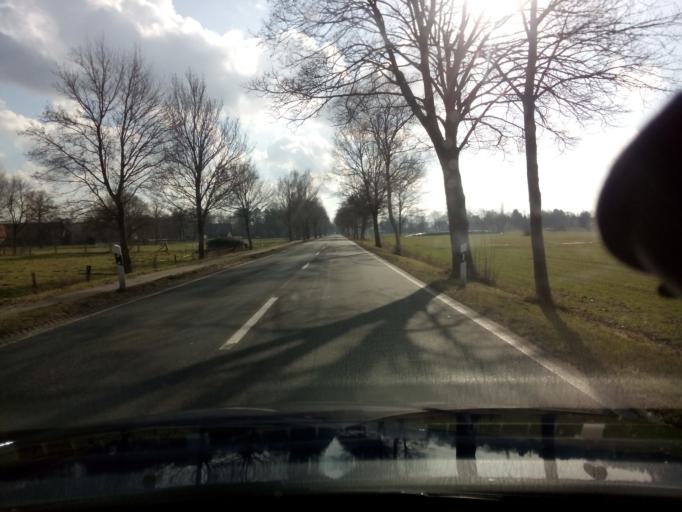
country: DE
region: Lower Saxony
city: Gnarrenburg
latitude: 53.3248
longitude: 8.9800
